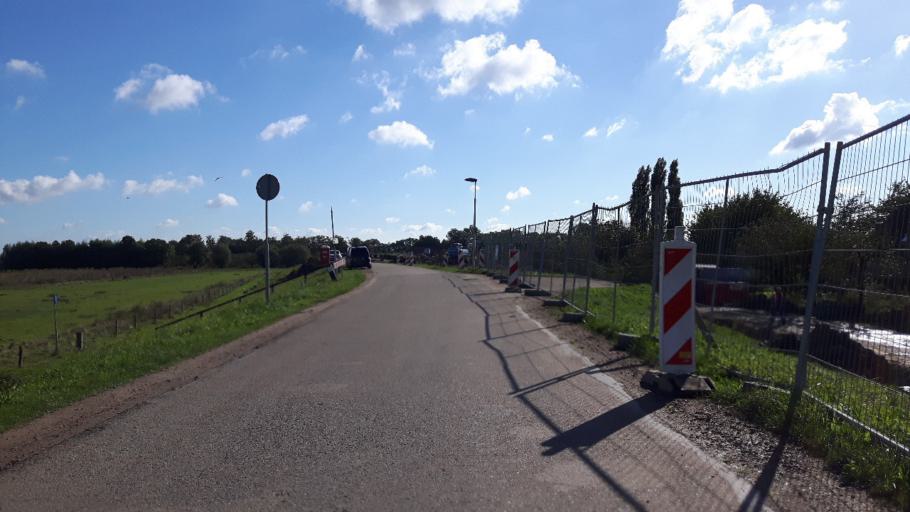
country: NL
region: Gelderland
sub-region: Gemeente Culemborg
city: Culemborg
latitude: 51.9601
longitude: 5.1823
